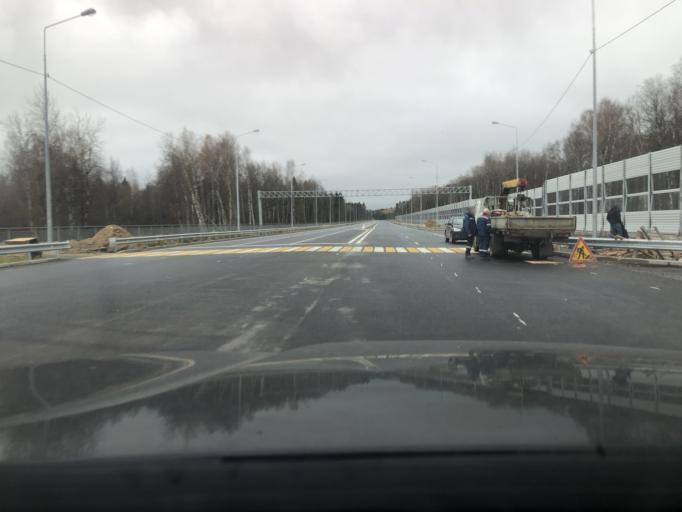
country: RU
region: Moskovskaya
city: Sergiyev Posad
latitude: 56.3371
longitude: 38.0935
